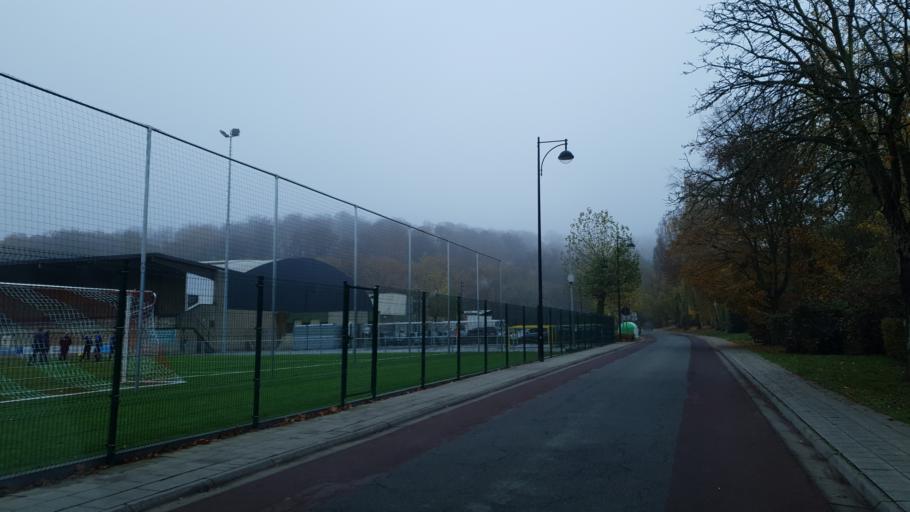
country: BE
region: Flanders
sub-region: Provincie Vlaams-Brabant
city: Kortenberg
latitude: 50.8843
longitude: 4.5460
